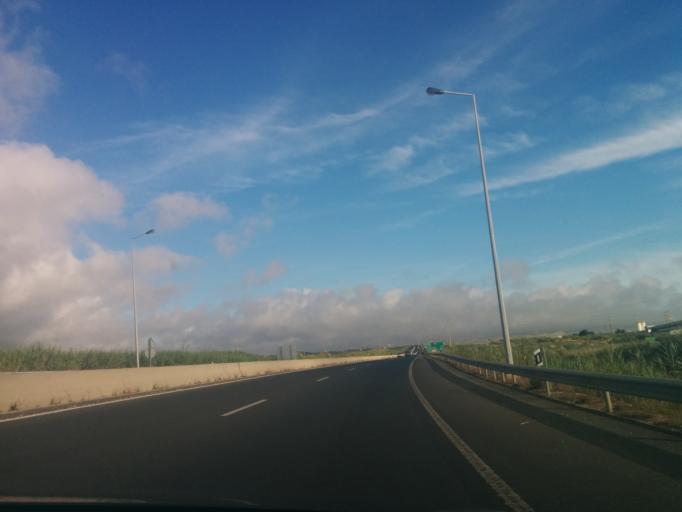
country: PT
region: Leiria
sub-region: Peniche
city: Atouguia da Baleia
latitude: 39.3444
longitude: -9.3406
